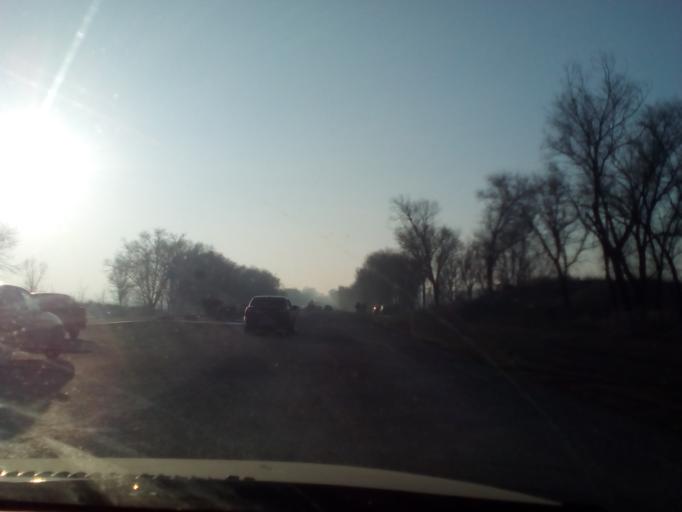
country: KZ
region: Almaty Oblysy
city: Burunday
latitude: 43.2232
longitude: 76.5911
